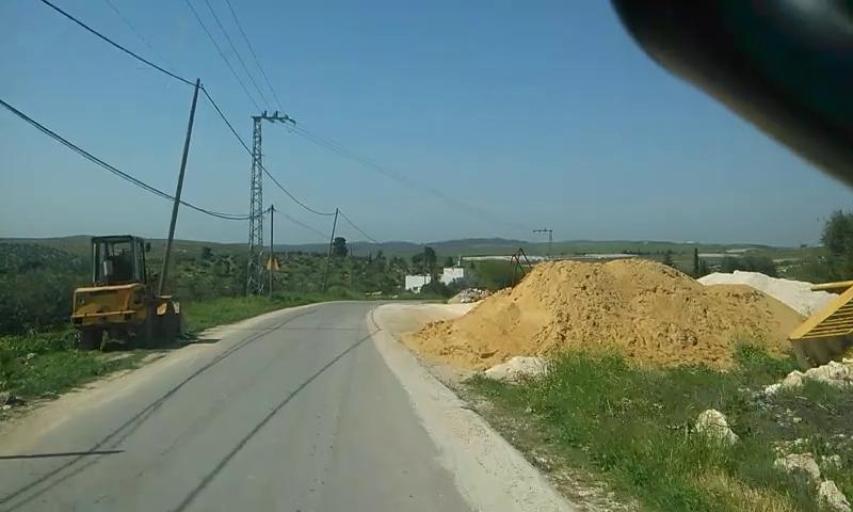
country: PS
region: West Bank
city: Al Majd
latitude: 31.4844
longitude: 34.9448
